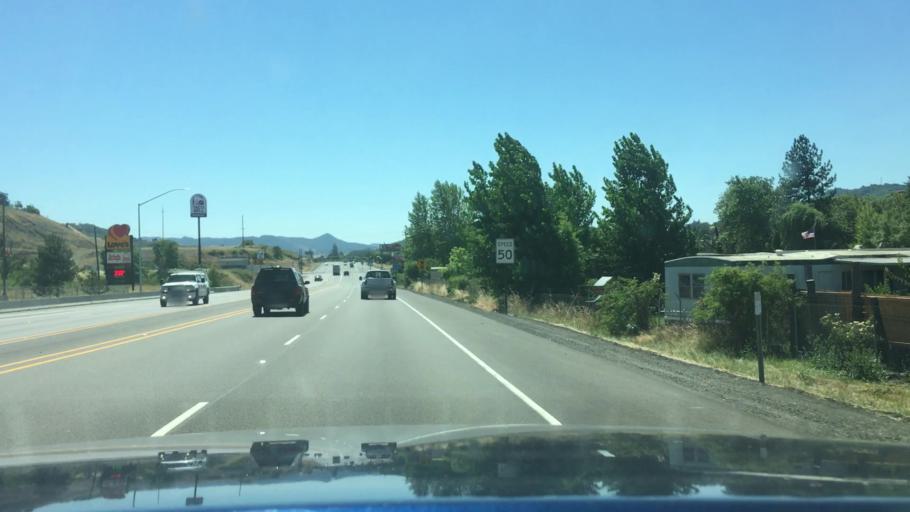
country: US
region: Oregon
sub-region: Douglas County
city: Green
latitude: 43.1515
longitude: -123.3680
